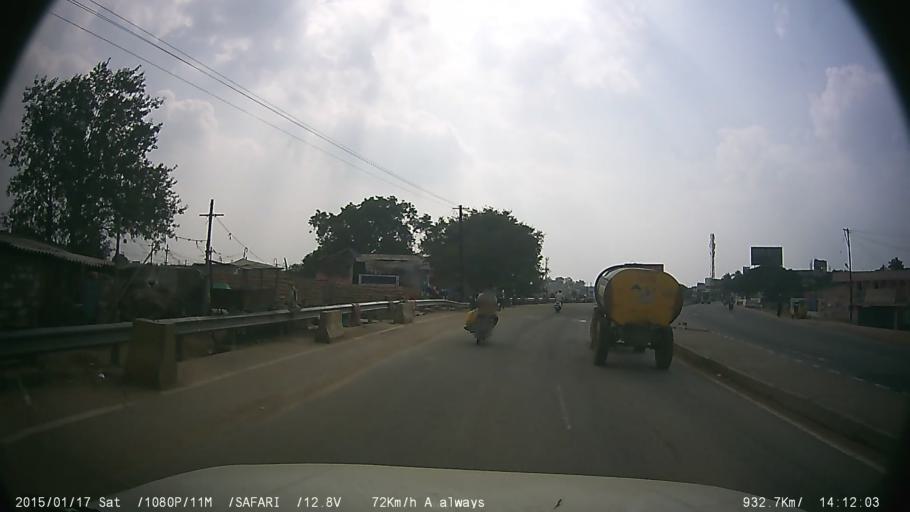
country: IN
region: Tamil Nadu
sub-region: Vellore
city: Ambur
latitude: 12.7899
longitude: 78.7266
